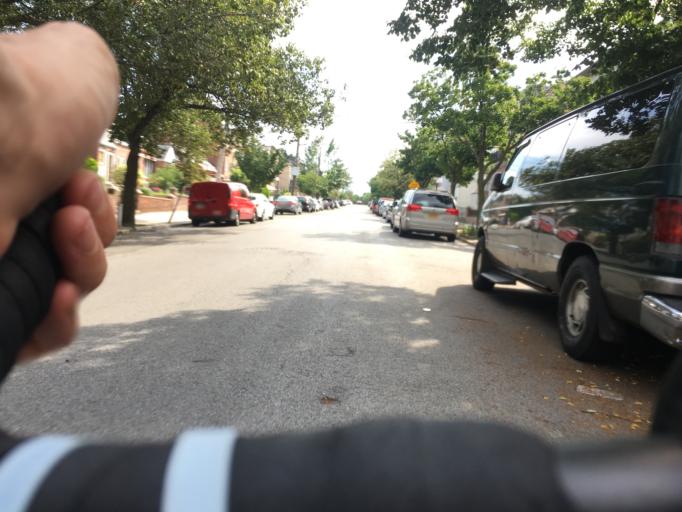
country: US
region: New York
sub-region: Queens County
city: Long Island City
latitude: 40.7753
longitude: -73.9005
